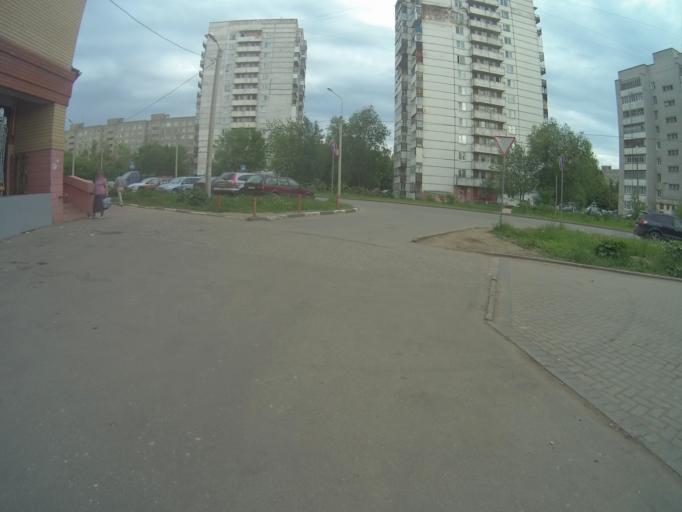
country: RU
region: Vladimir
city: Kommunar
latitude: 56.1618
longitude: 40.4613
